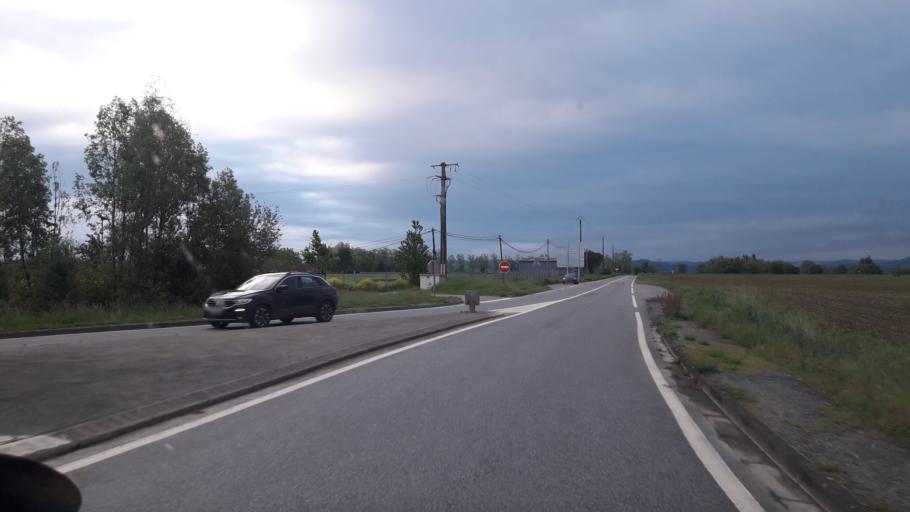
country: FR
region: Midi-Pyrenees
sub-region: Departement de la Haute-Garonne
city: Cazeres
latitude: 43.2356
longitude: 1.0782
